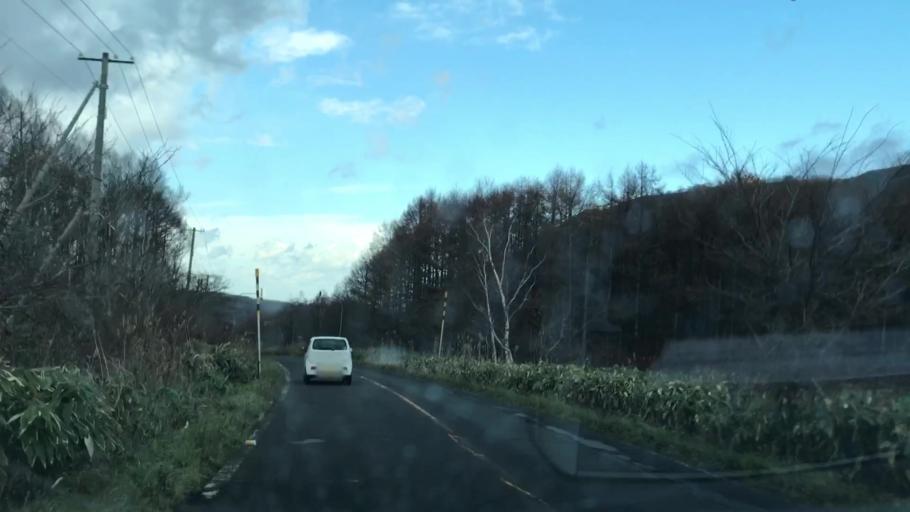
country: JP
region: Hokkaido
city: Yoichi
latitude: 43.3291
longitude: 140.4916
